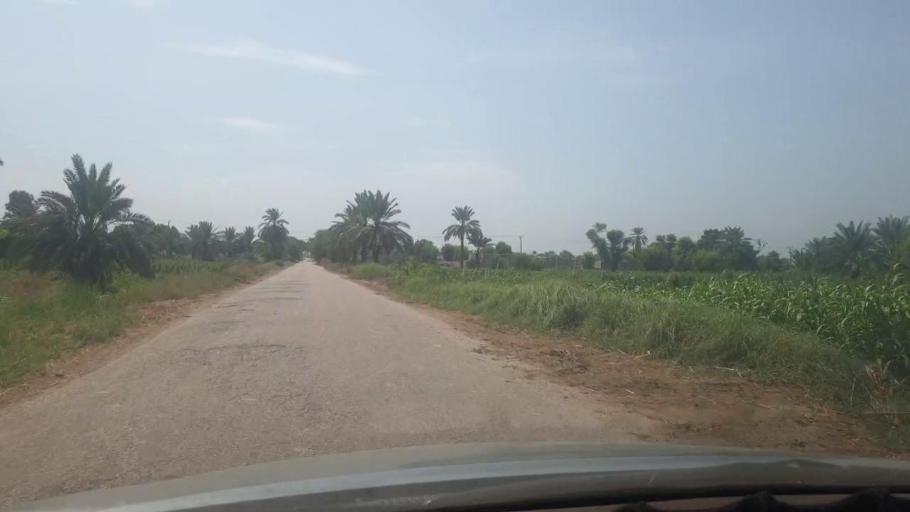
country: PK
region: Sindh
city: Bozdar
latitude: 27.2095
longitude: 68.5772
